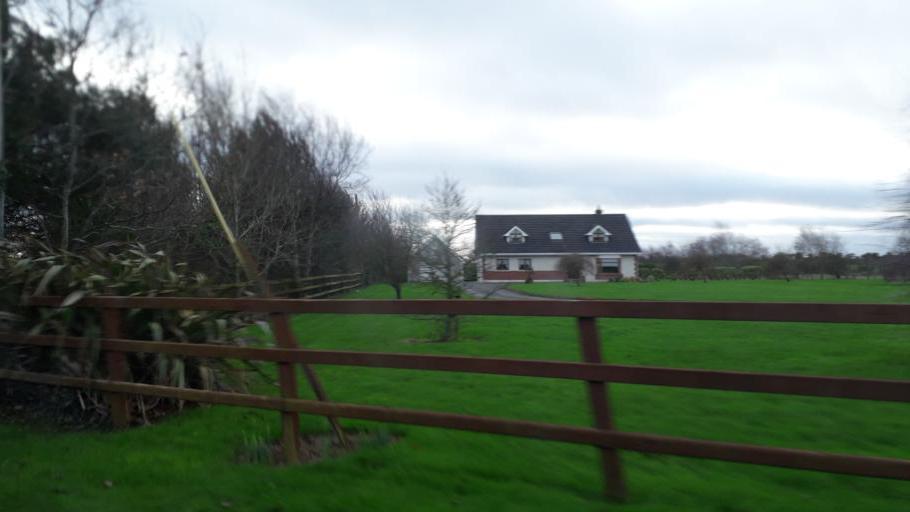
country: IE
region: Leinster
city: An Ros
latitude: 53.5491
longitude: -6.1181
